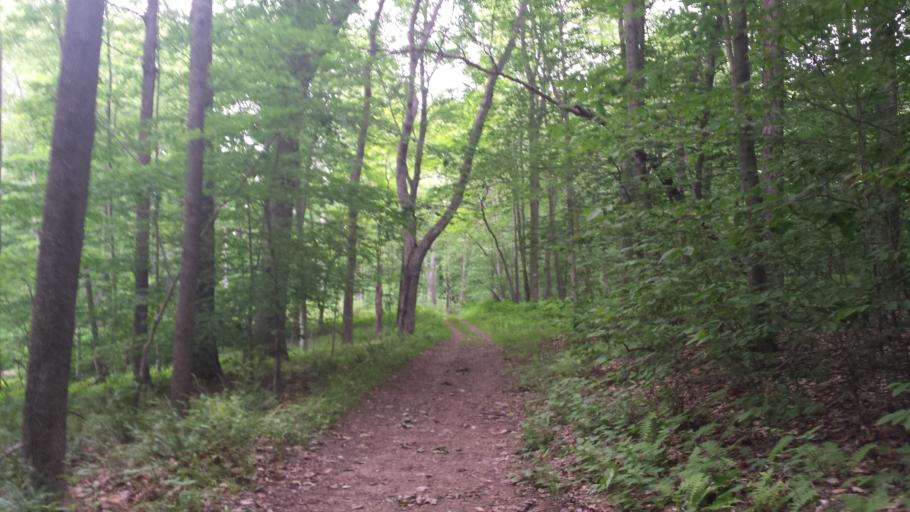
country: US
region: New York
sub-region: Westchester County
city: Pound Ridge
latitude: 41.2703
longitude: -73.5838
